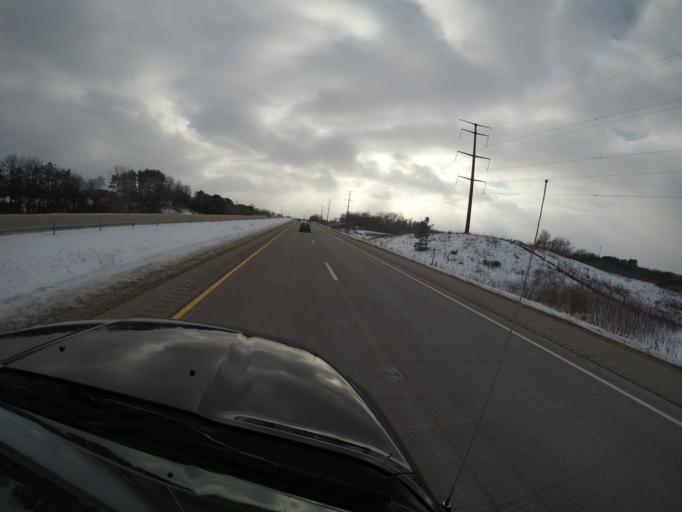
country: US
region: Wisconsin
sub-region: La Crosse County
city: Holmen
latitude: 43.9887
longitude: -91.2864
